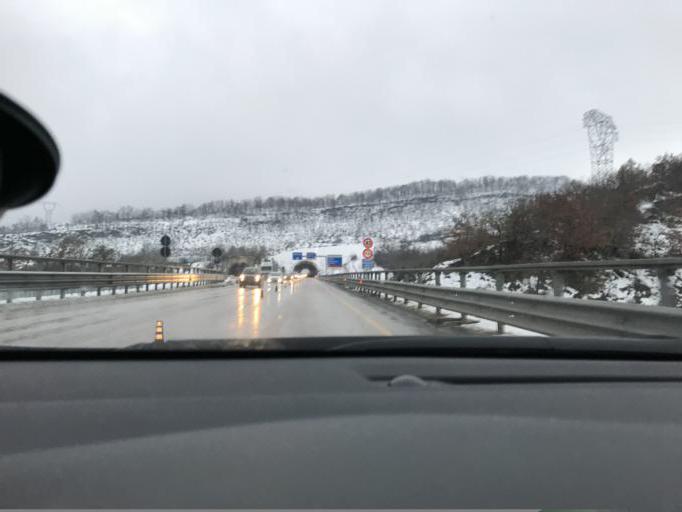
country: IT
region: Umbria
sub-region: Provincia di Perugia
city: Fossato di Vico
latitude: 43.3030
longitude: 12.8343
